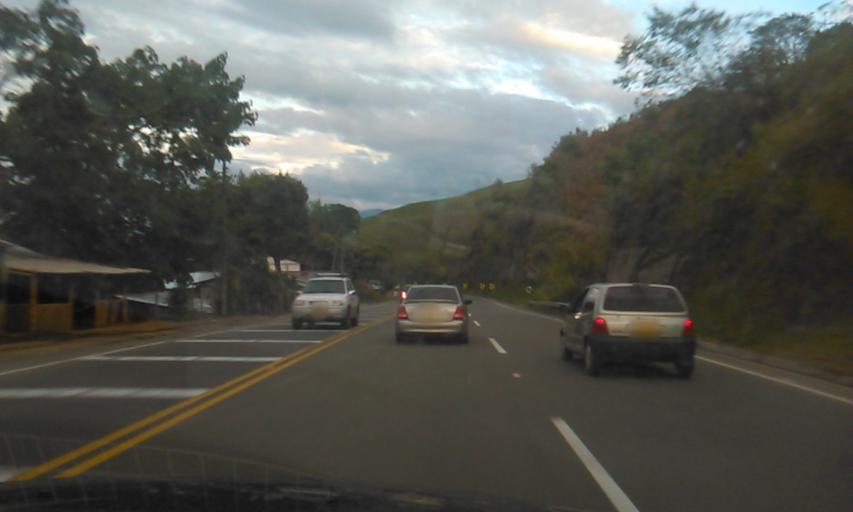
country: CO
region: Valle del Cauca
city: Caicedonia
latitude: 4.4082
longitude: -75.8924
